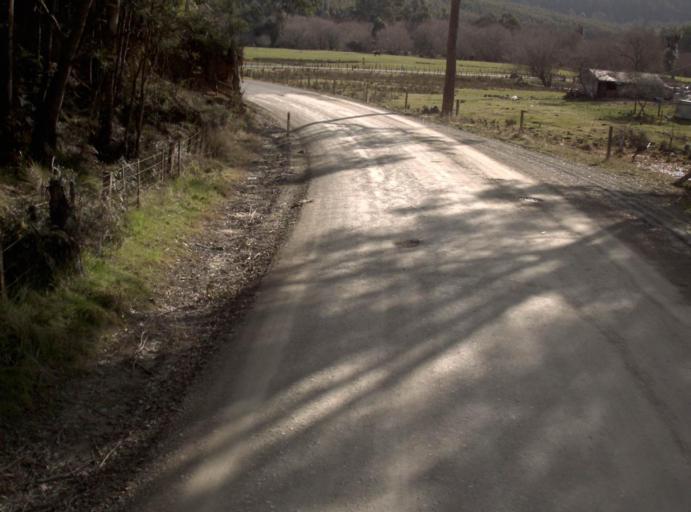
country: AU
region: Tasmania
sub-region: Dorset
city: Scottsdale
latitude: -41.2863
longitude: 147.3859
